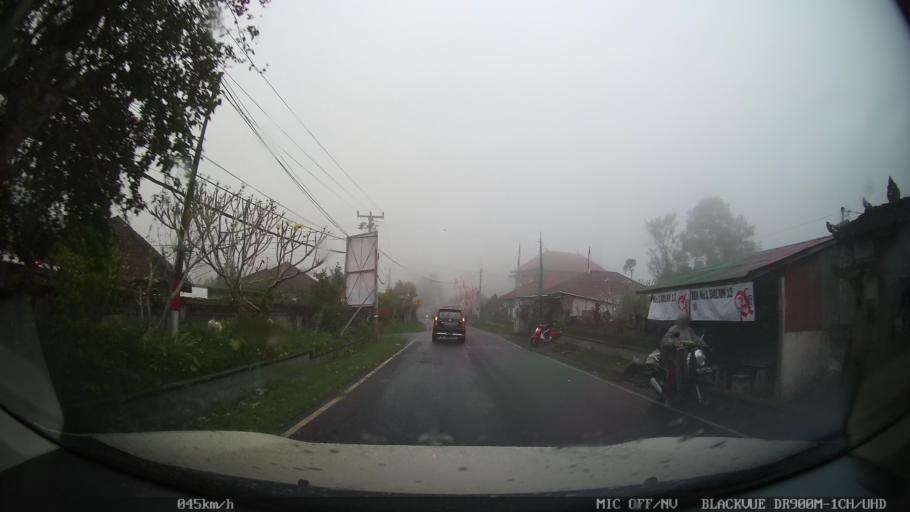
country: ID
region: Bali
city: Banjar Taro Kelod
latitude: -8.3360
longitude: 115.2849
